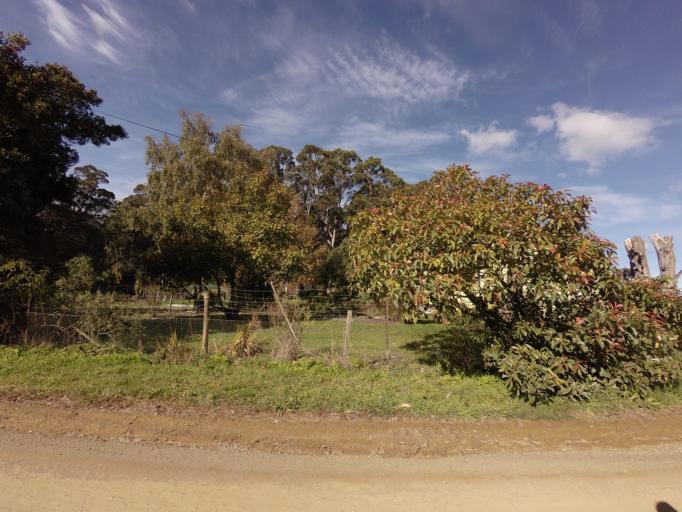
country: AU
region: Tasmania
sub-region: Clarence
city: Sandford
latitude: -43.1432
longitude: 147.7654
